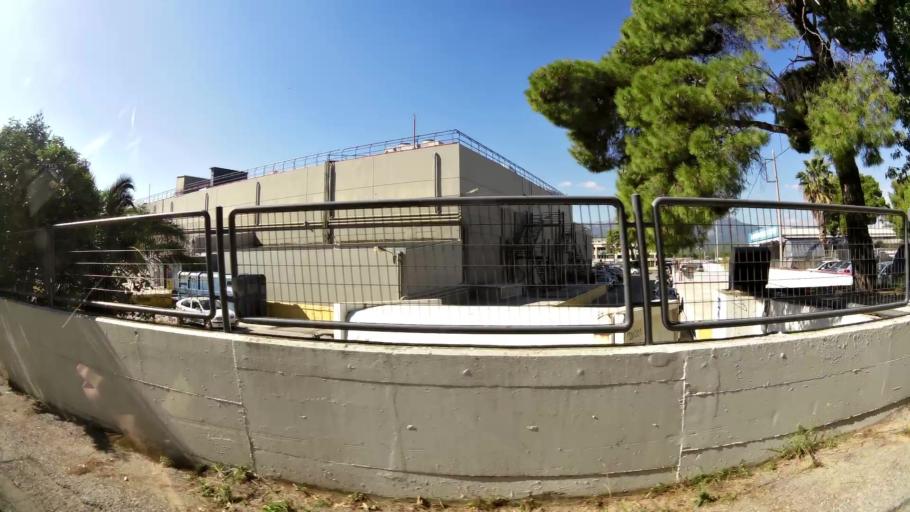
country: GR
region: Attica
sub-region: Nomarchia Athinas
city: Ekali
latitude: 38.1149
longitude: 23.8291
